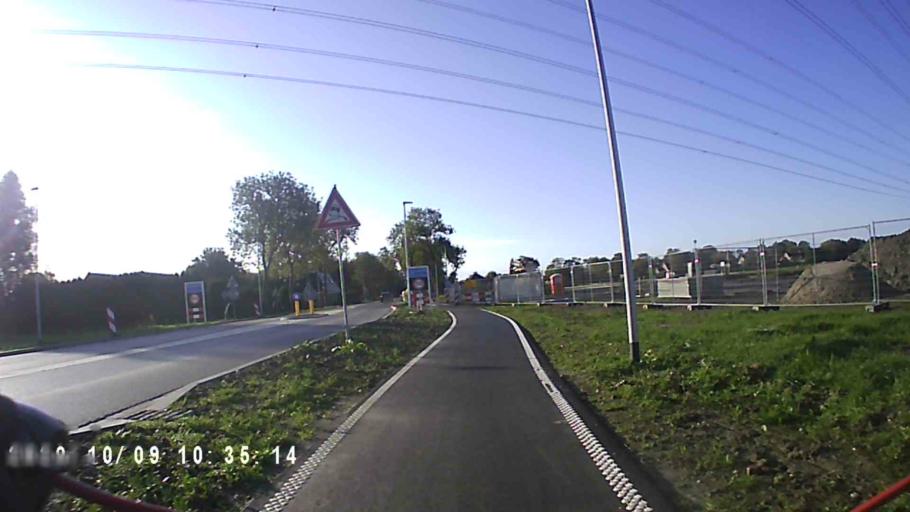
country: NL
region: Groningen
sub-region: Gemeente Winsum
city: Winsum
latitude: 53.2988
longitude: 6.5338
